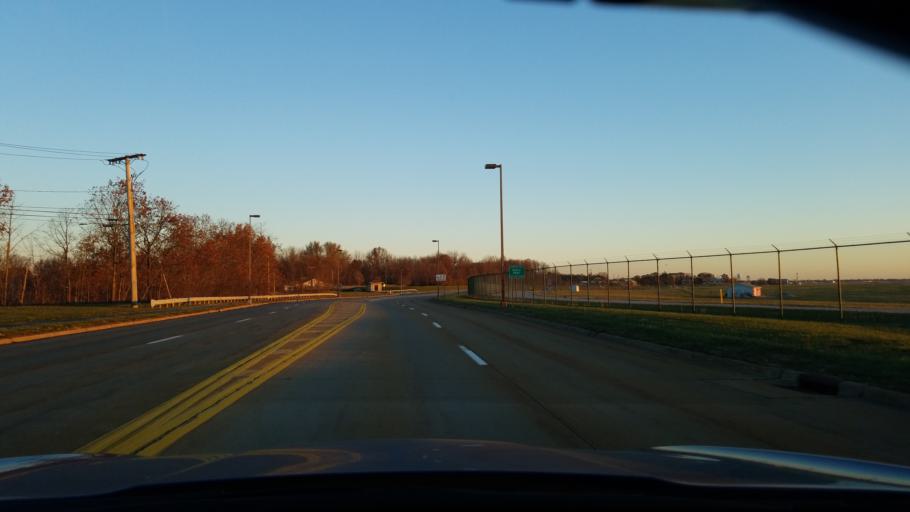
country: US
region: Ohio
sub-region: Cuyahoga County
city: Olmsted Falls
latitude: 41.3969
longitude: -81.8793
